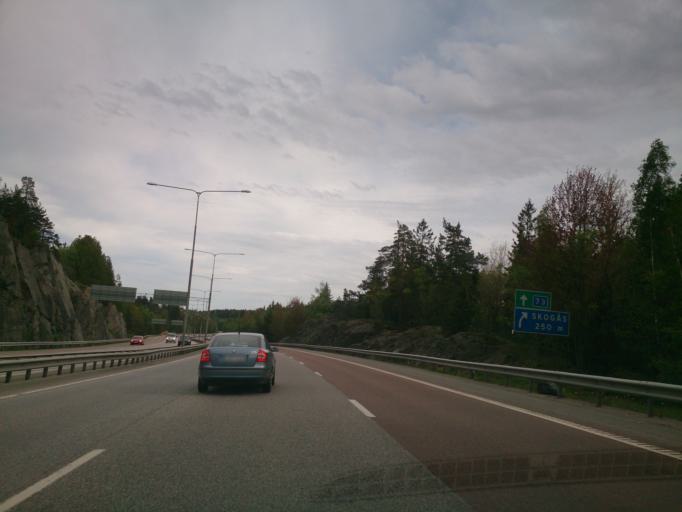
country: SE
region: Stockholm
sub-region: Haninge Kommun
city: Handen
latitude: 59.2260
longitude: 18.1271
